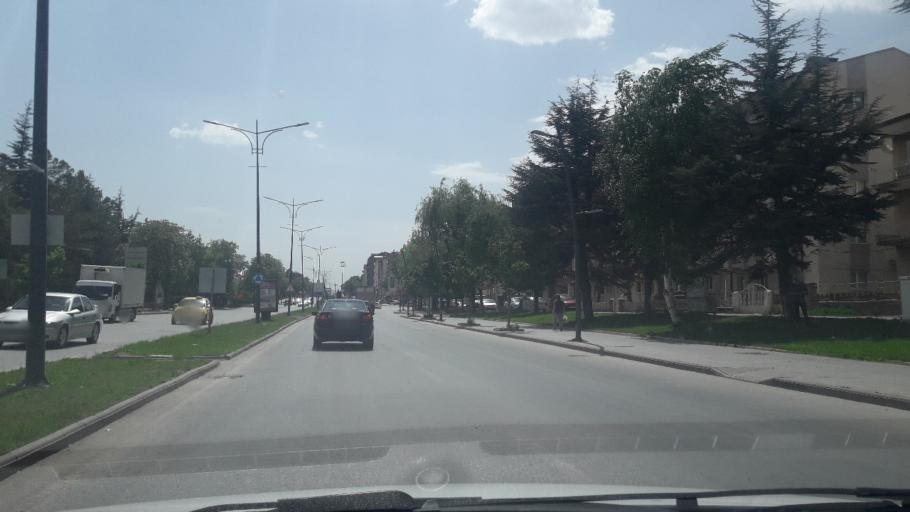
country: TR
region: Sivas
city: Sivas
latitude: 39.7360
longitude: 36.9949
